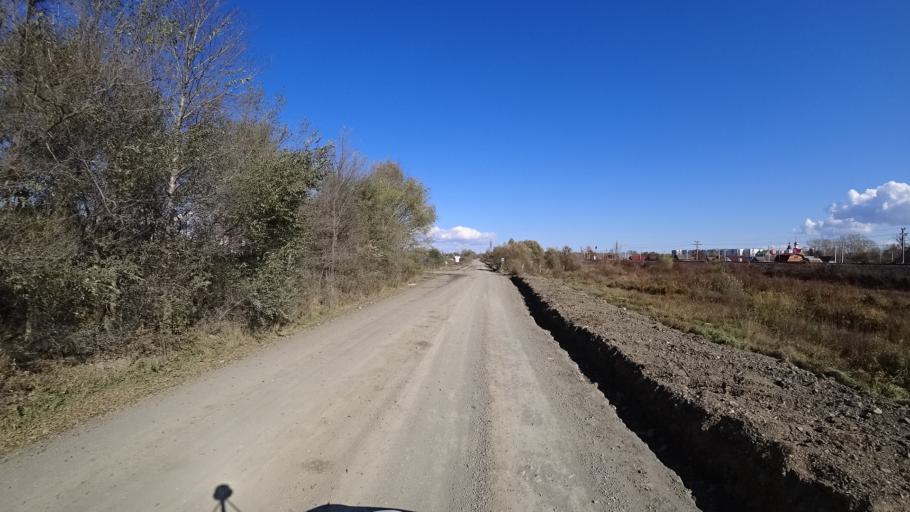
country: RU
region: Khabarovsk Krai
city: Amursk
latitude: 50.1012
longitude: 136.5070
